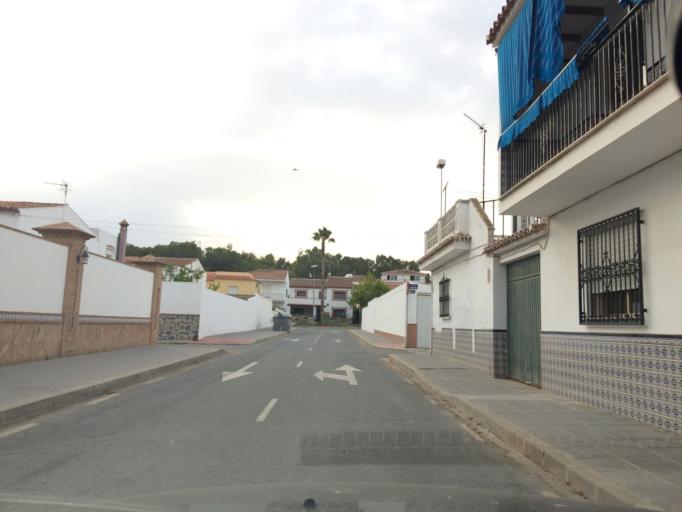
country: ES
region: Andalusia
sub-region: Provincia de Malaga
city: Estacion de Cartama
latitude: 36.7303
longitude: -4.5720
